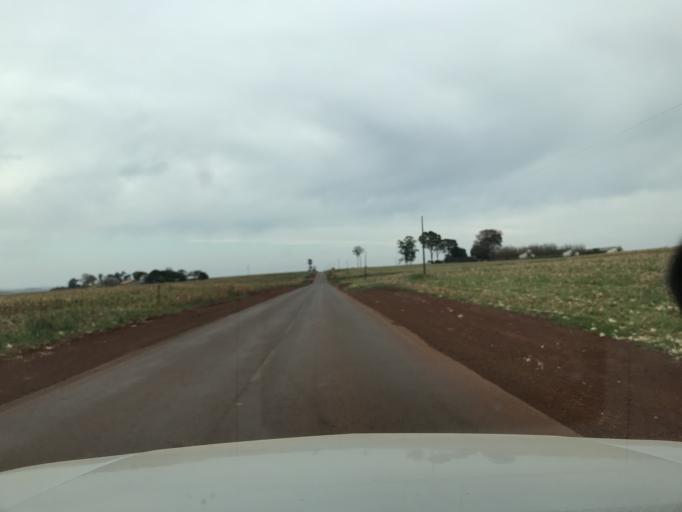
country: BR
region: Parana
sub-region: Palotina
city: Palotina
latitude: -24.4200
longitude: -53.8891
